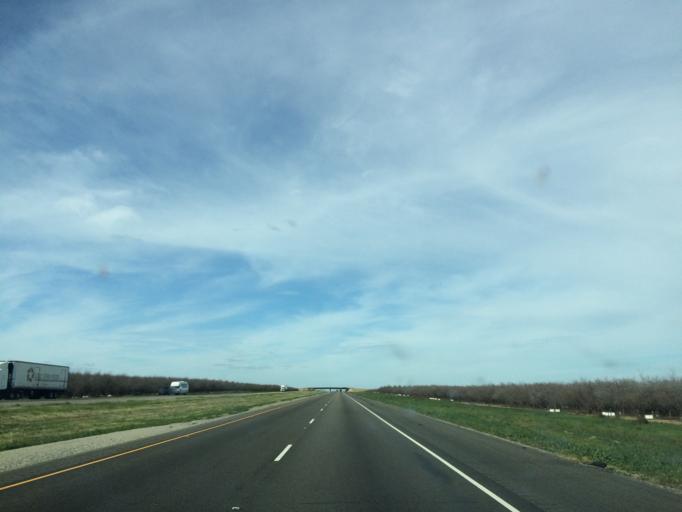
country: US
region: California
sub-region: Merced County
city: South Dos Palos
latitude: 36.7515
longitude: -120.7056
